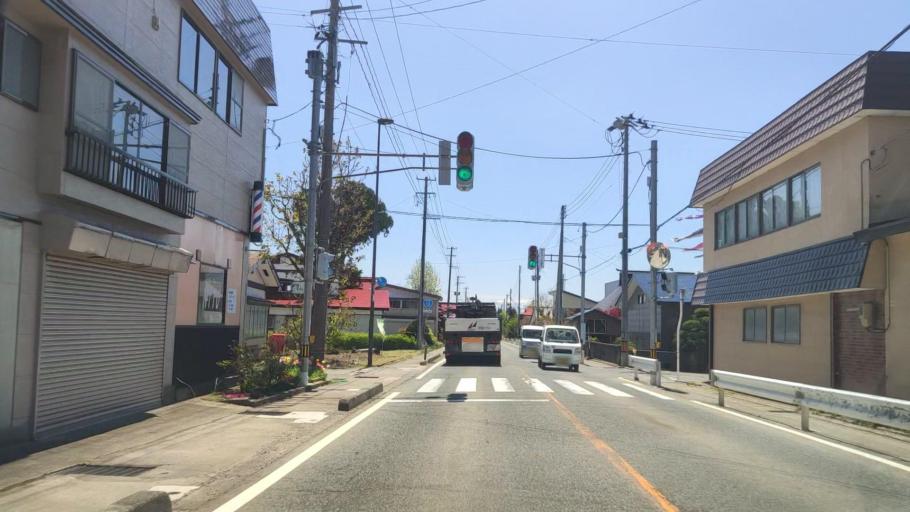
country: JP
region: Yamagata
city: Shinjo
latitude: 38.8045
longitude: 140.3210
